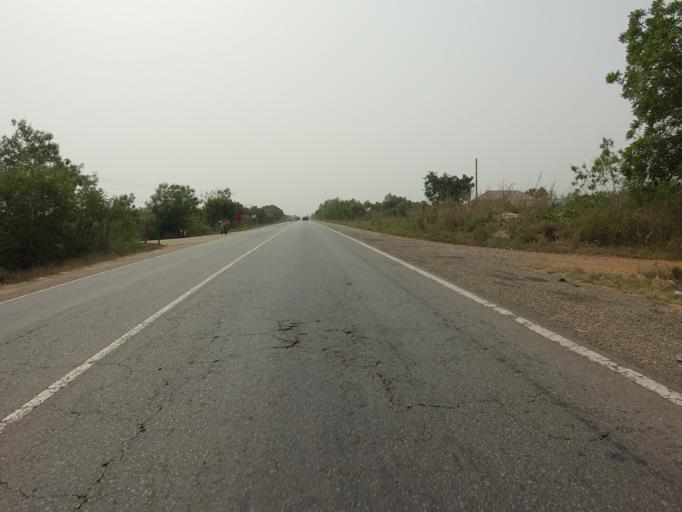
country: GH
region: Volta
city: Anloga
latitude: 5.9504
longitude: 0.5240
